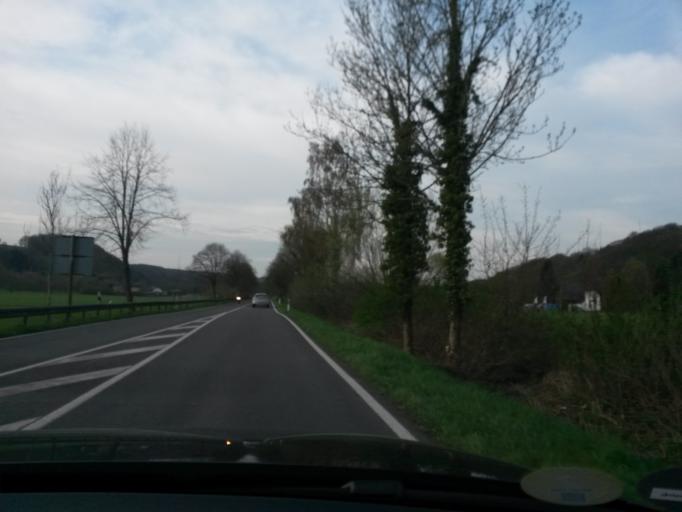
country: DE
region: North Rhine-Westphalia
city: Lohmar
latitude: 50.8774
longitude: 7.2492
